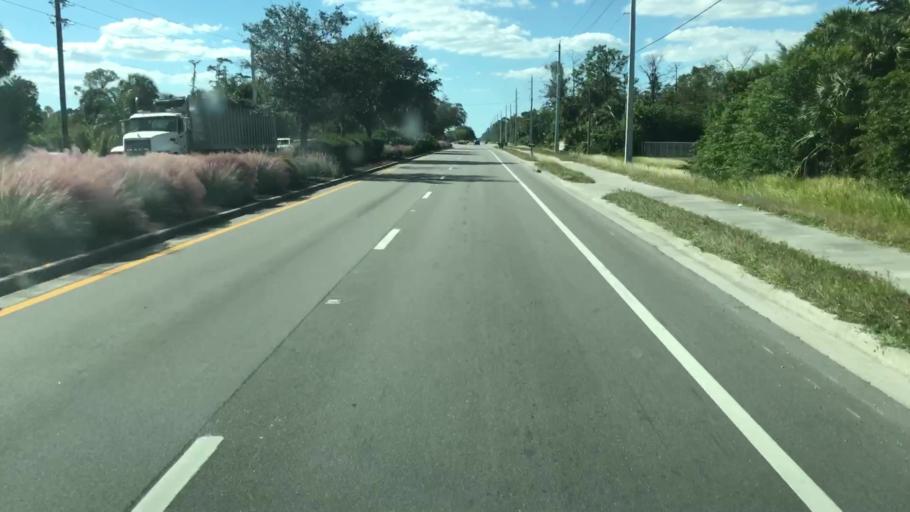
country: US
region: Florida
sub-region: Collier County
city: Orangetree
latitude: 26.2298
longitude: -81.6179
